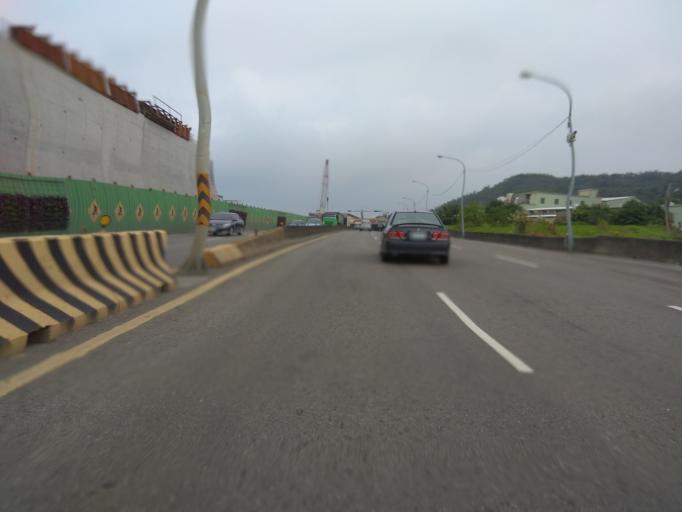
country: TW
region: Taiwan
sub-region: Hsinchu
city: Zhubei
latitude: 24.8751
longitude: 120.9542
